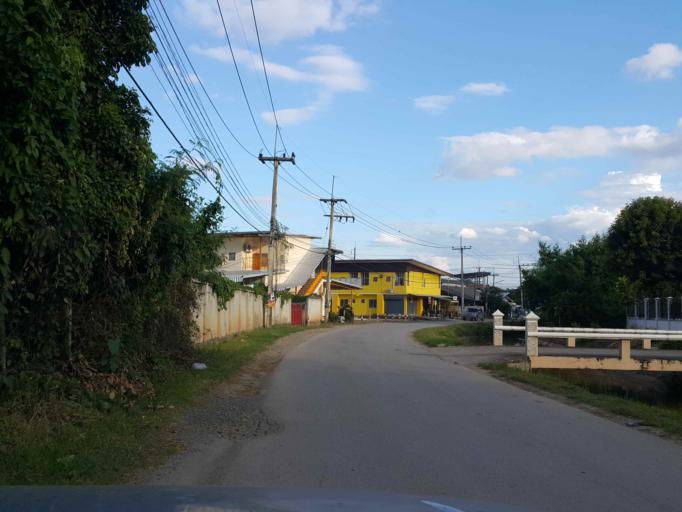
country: TH
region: Chiang Mai
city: San Sai
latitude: 18.9181
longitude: 98.9751
